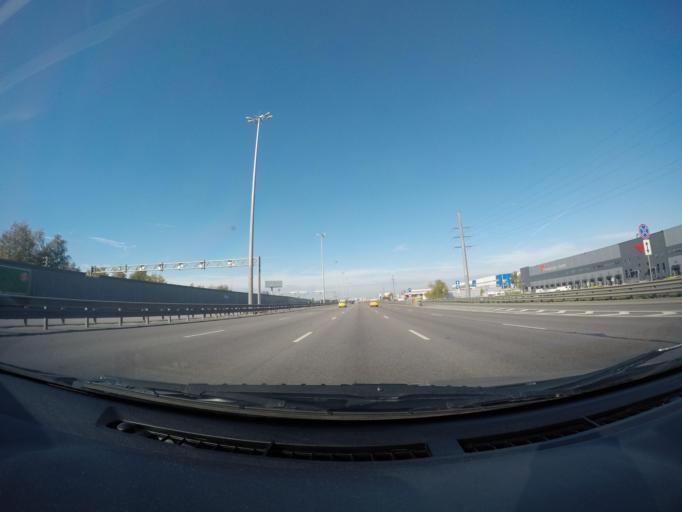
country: RU
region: Moskovskaya
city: Tomilino
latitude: 55.6417
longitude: 37.9195
